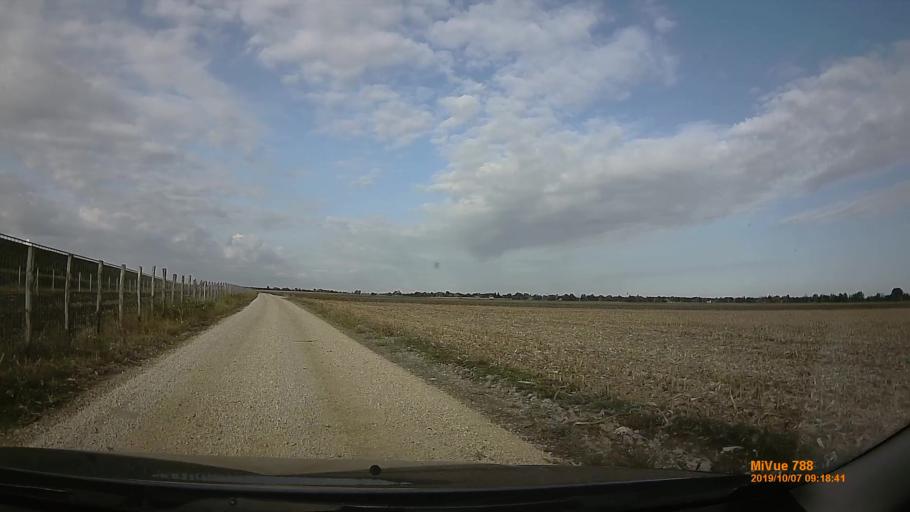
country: HU
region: Bekes
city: Nagyszenas
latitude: 46.8136
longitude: 20.6693
